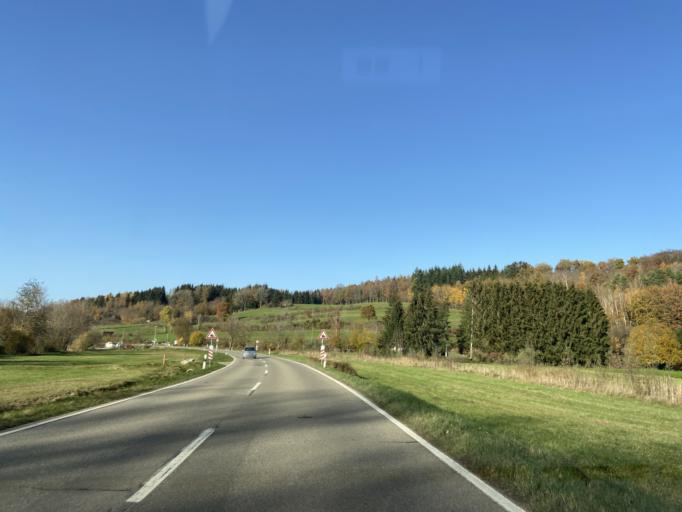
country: DE
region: Baden-Wuerttemberg
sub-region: Tuebingen Region
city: Ennetach
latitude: 48.0359
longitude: 9.2876
